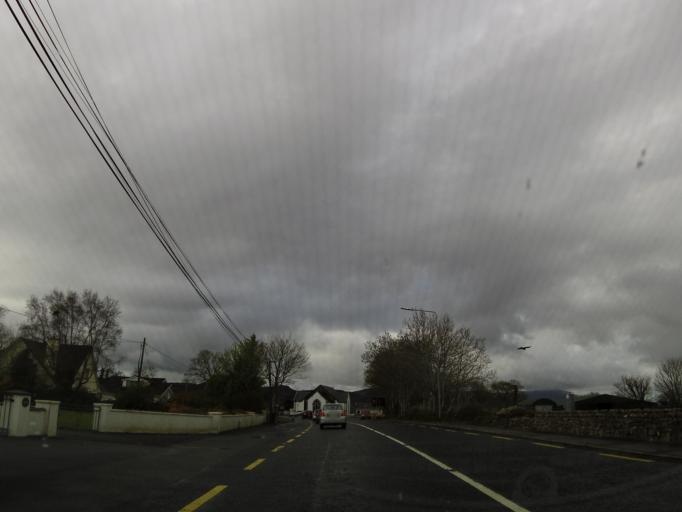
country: IE
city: Ballisodare
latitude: 54.2089
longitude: -8.5315
